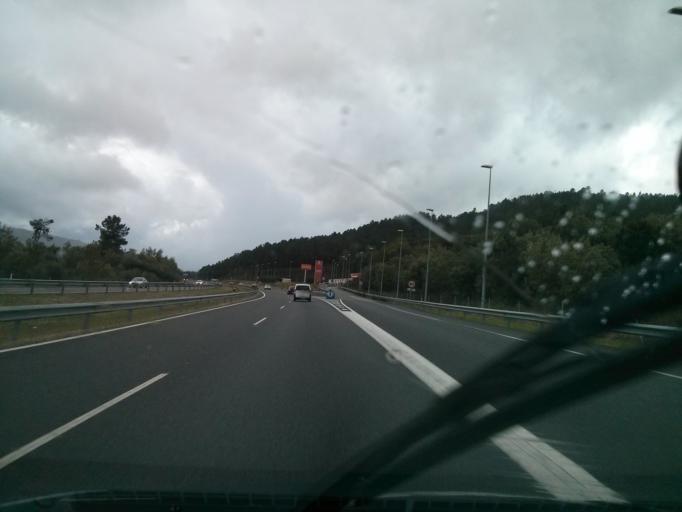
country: ES
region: Galicia
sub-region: Provincia de Ourense
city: Cenlle
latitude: 42.3158
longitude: -8.0905
